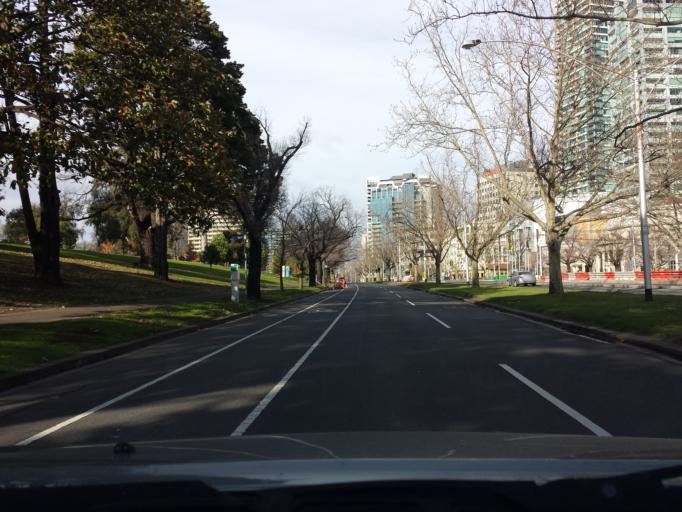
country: AU
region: Victoria
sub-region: Port Phillip
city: South Melbourne
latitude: -37.8291
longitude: 144.9715
